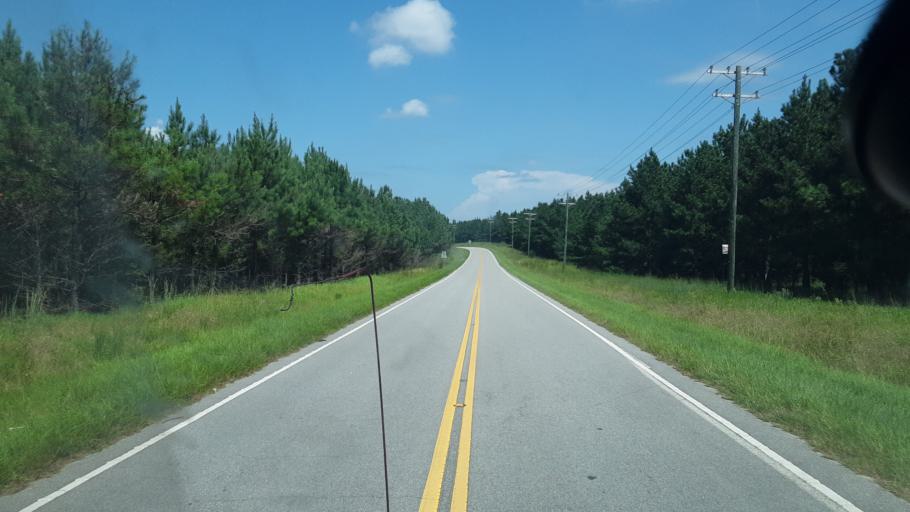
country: US
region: South Carolina
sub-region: Bamberg County
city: Bamberg
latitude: 33.4087
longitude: -81.0164
